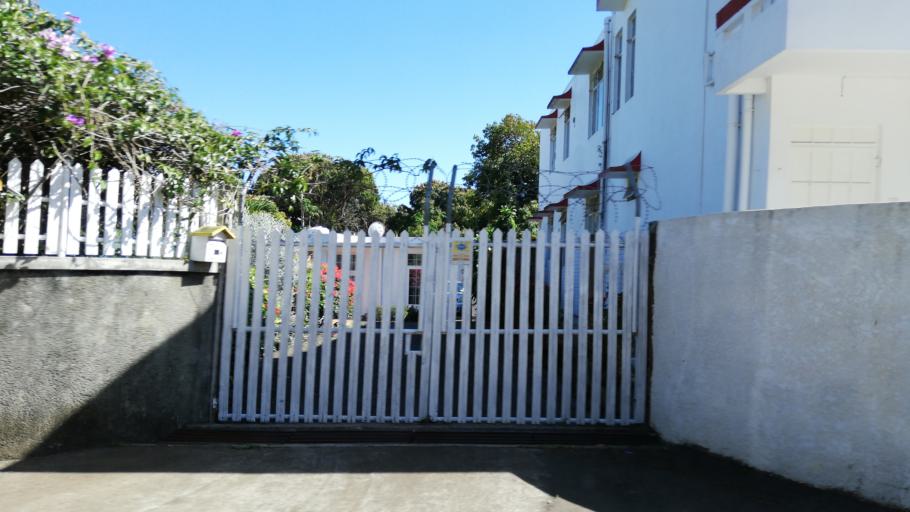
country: MU
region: Plaines Wilhems
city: Ebene
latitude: -20.2351
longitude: 57.4732
